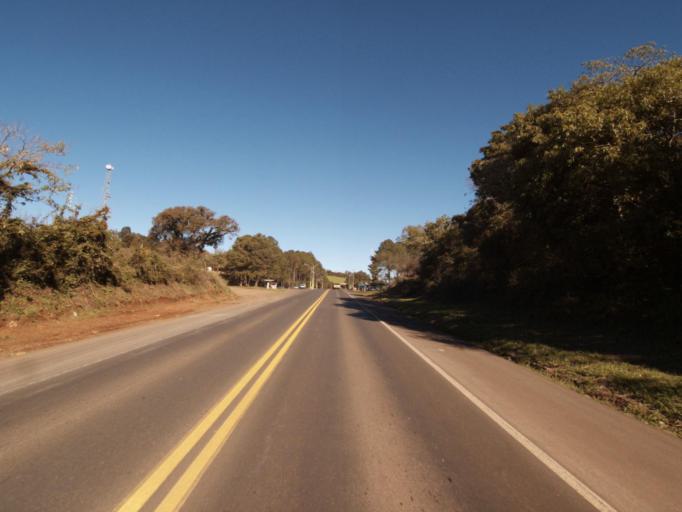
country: BR
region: Santa Catarina
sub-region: Xanxere
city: Xanxere
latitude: -26.8999
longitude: -52.4633
